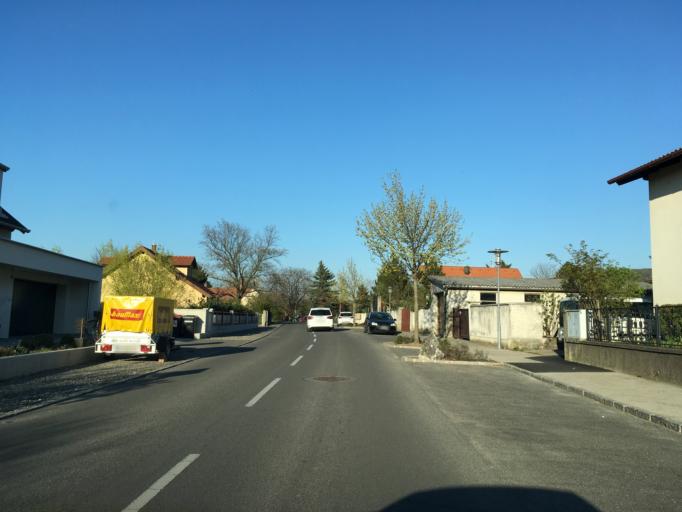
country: AT
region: Lower Austria
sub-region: Politischer Bezirk Tulln
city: Konigstetten
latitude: 48.3036
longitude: 16.1485
